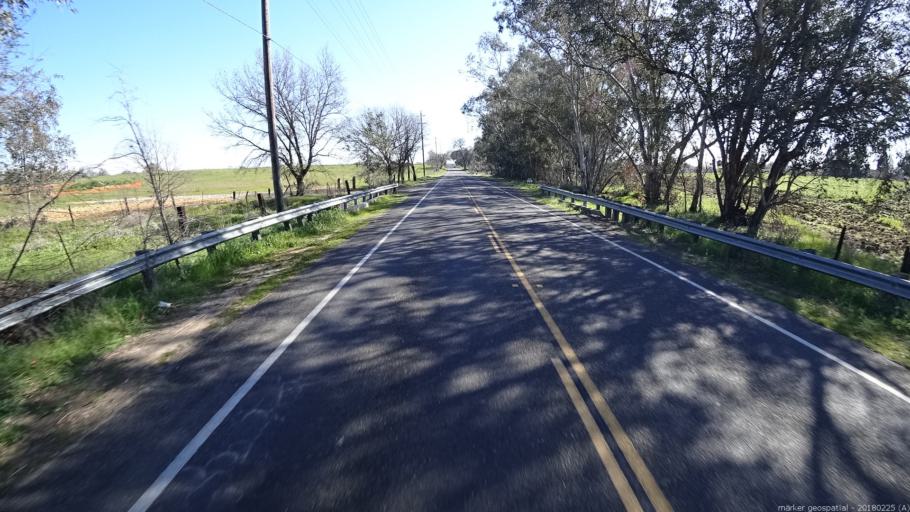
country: US
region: California
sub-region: Sacramento County
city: North Highlands
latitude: 38.7288
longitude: -121.3764
